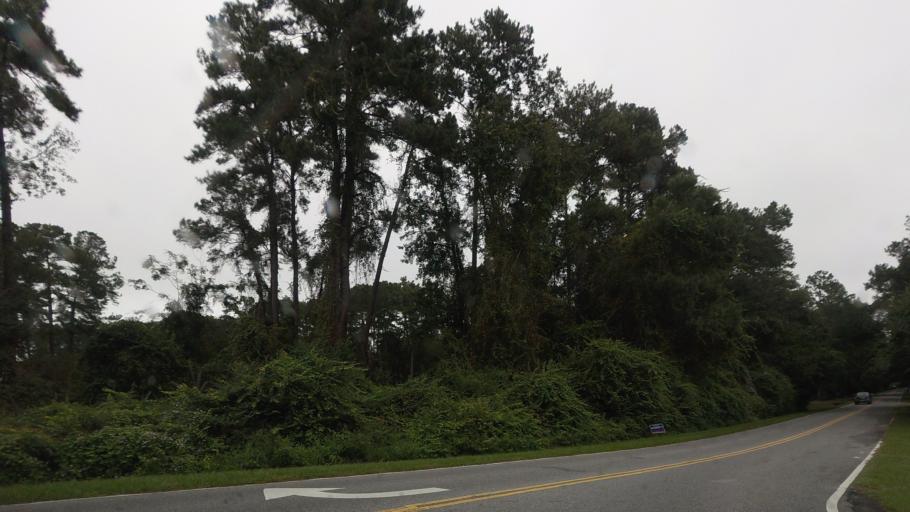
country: US
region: Georgia
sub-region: Lowndes County
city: Remerton
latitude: 30.8853
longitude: -83.3127
